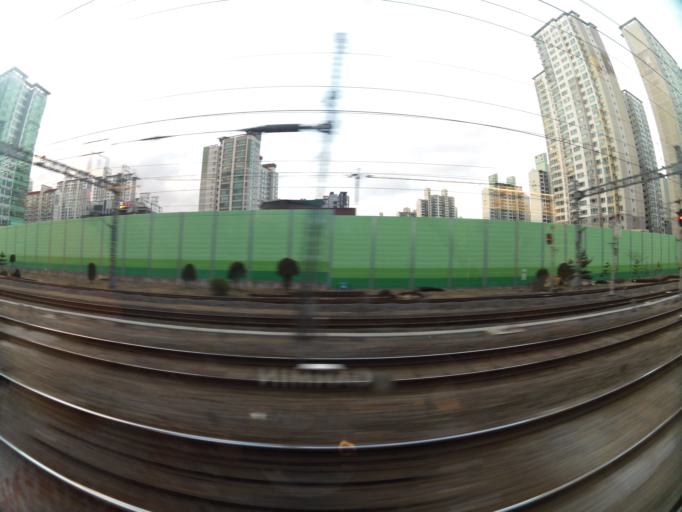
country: KR
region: Gyeonggi-do
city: Kwangmyong
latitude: 37.5056
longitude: 126.8857
